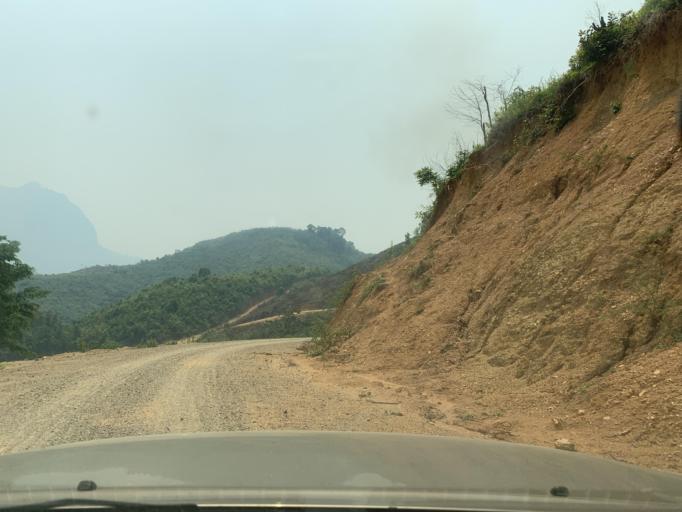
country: LA
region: Louangphabang
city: Louangphabang
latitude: 19.8614
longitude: 102.2571
